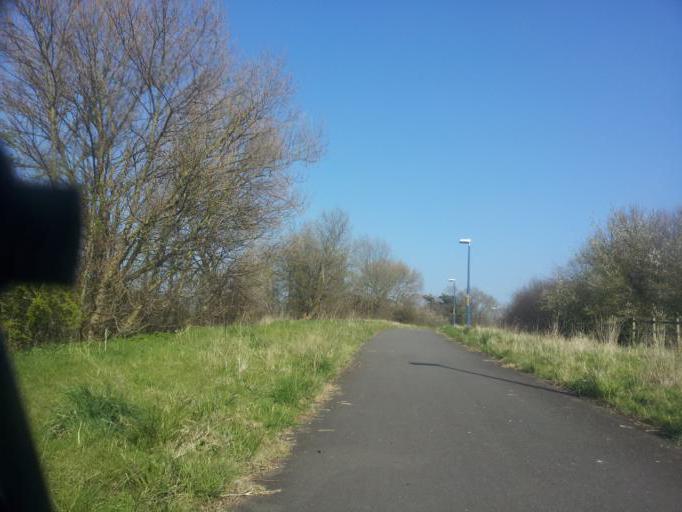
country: GB
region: England
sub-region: Kent
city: Gravesend
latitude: 51.4098
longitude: 0.3847
